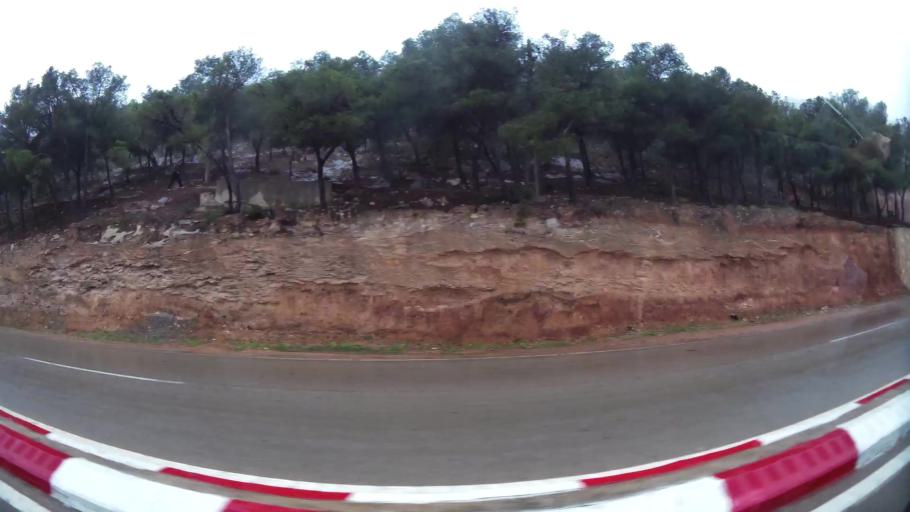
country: MA
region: Taza-Al Hoceima-Taounate
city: Tirhanimine
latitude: 35.2220
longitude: -3.9273
